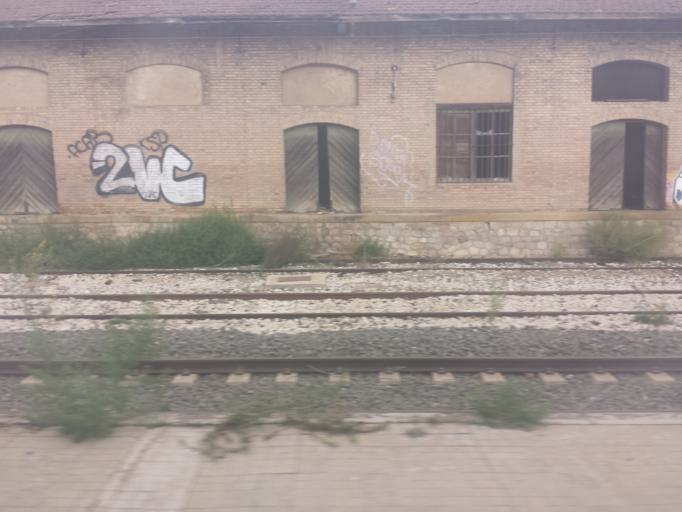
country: ES
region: Aragon
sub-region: Provincia de Zaragoza
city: Sobradiel
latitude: 41.7230
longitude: -1.0198
